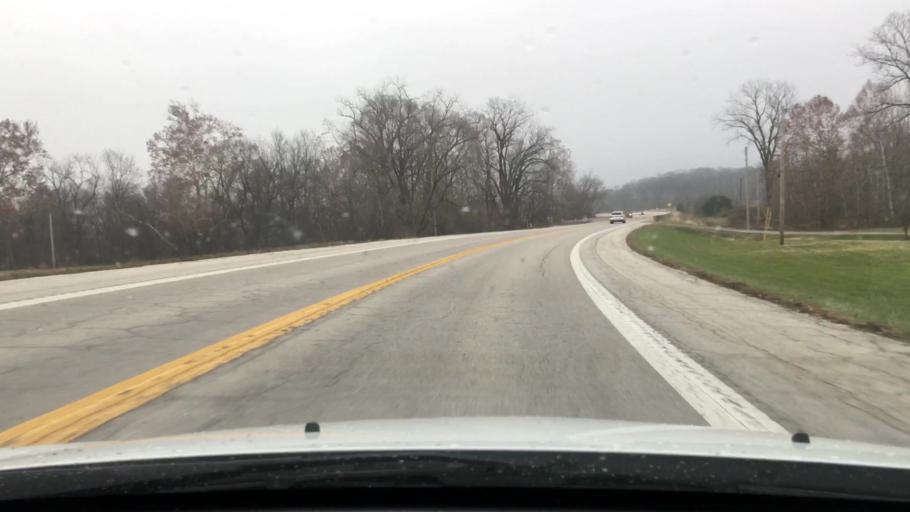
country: US
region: Missouri
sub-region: Pike County
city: Bowling Green
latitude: 39.3792
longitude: -91.1494
